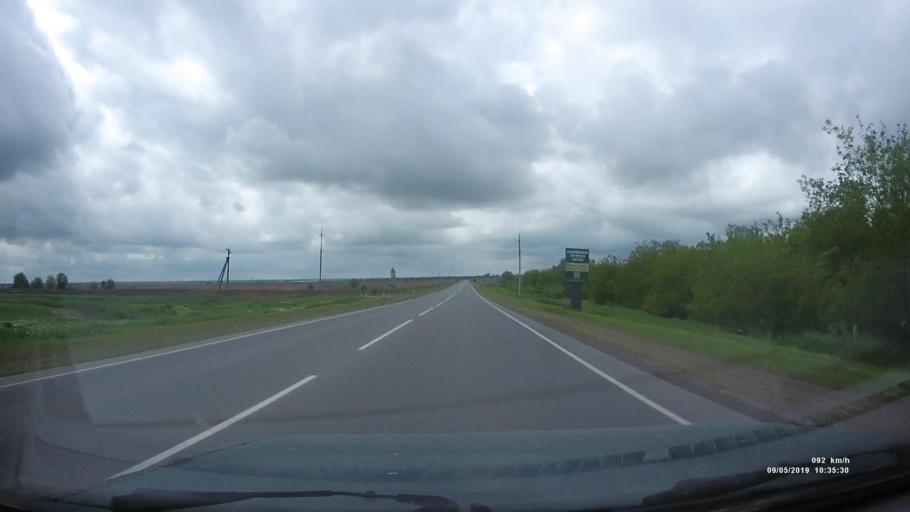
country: RU
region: Rostov
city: Peshkovo
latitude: 47.0420
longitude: 39.4134
